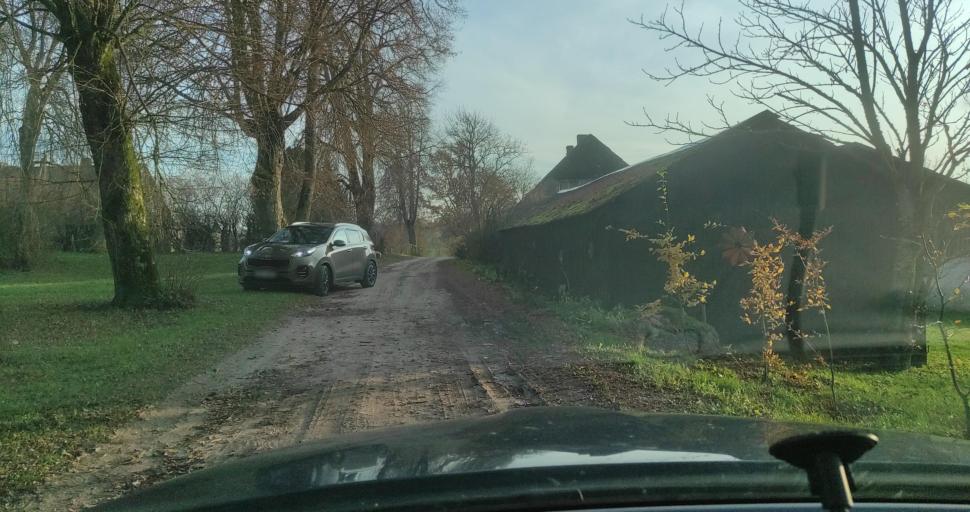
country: LV
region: Aizpute
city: Aizpute
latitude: 56.7510
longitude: 21.7972
